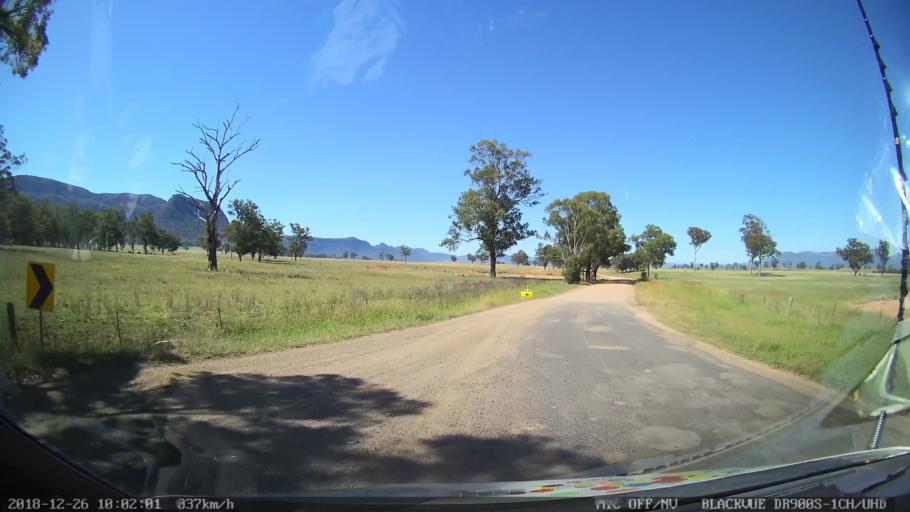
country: AU
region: New South Wales
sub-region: Mid-Western Regional
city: Kandos
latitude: -33.0506
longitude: 150.2231
